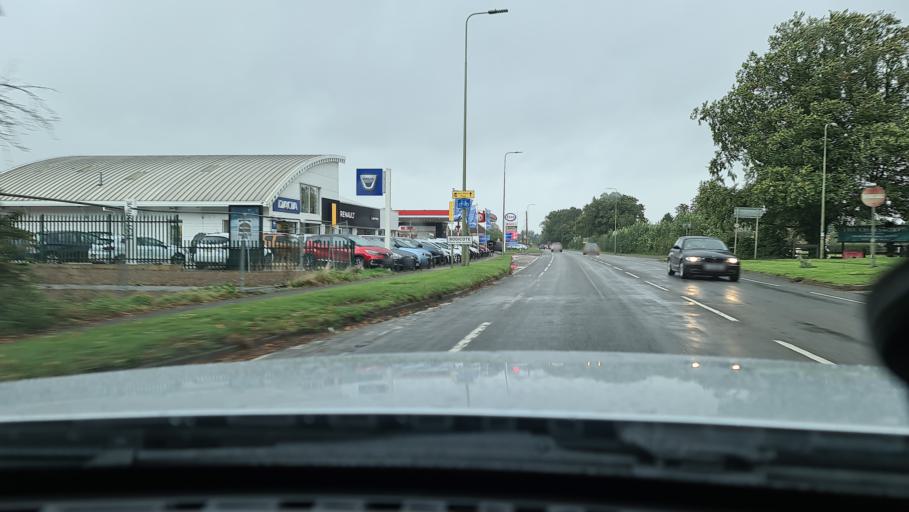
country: GB
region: England
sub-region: Oxfordshire
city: Banbury
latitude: 52.0433
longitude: -1.3290
